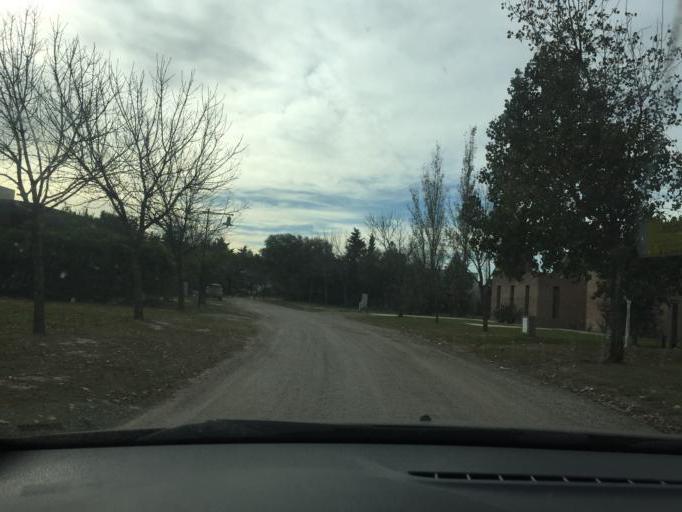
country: AR
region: Cordoba
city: Villa Allende
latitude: -31.2990
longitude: -64.2374
